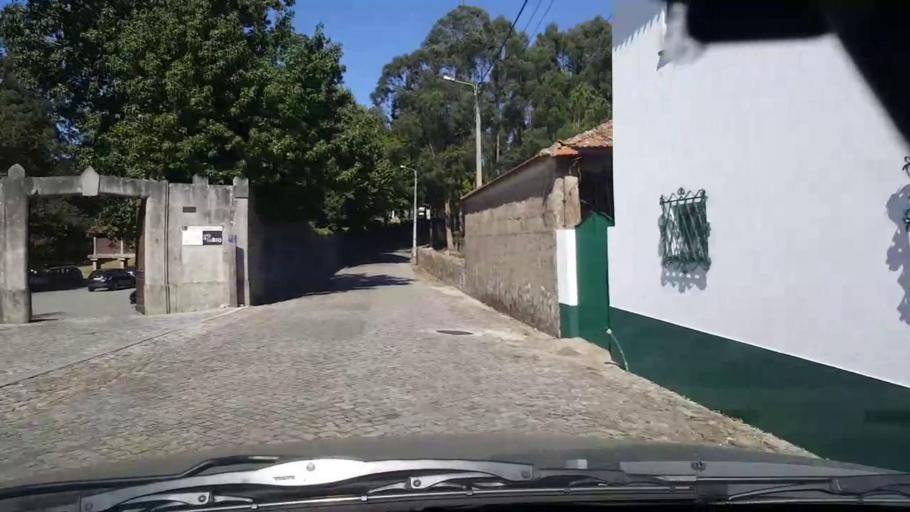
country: PT
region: Porto
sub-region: Vila do Conde
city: Arvore
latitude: 41.3272
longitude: -8.6731
